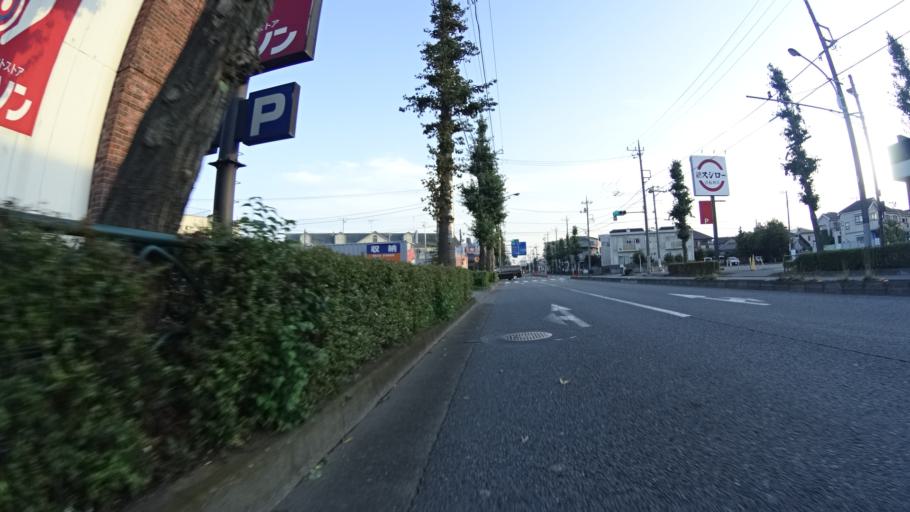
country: JP
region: Tokyo
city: Fussa
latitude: 35.7183
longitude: 139.3355
